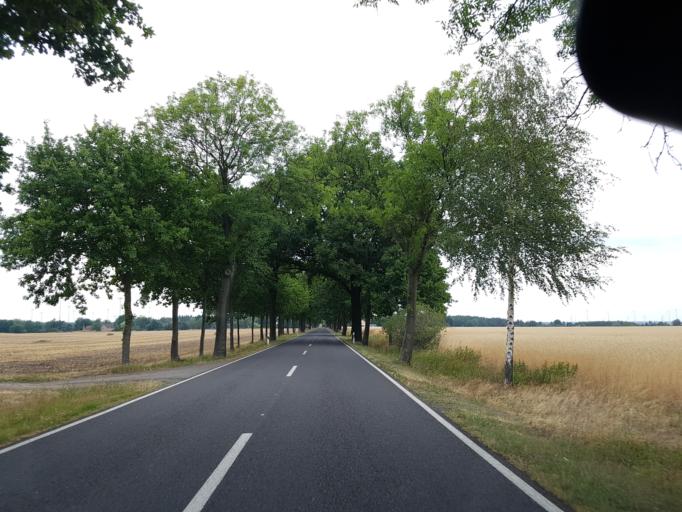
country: DE
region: Brandenburg
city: Sallgast
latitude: 51.6025
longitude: 13.8454
